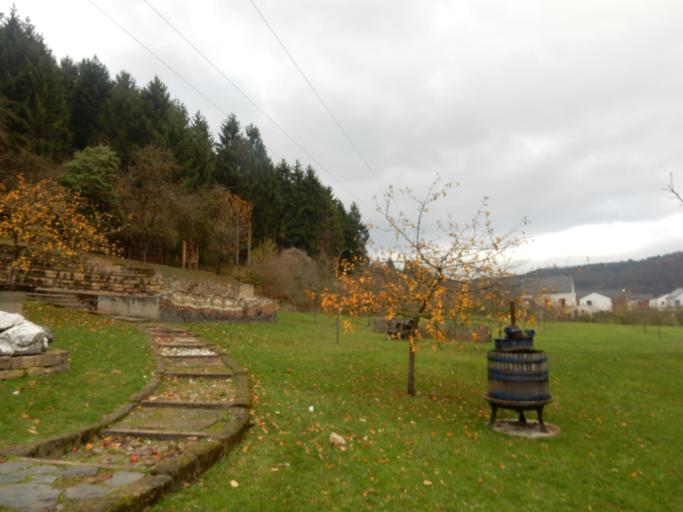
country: LU
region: Grevenmacher
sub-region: Canton d'Echternach
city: Mompach
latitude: 49.7561
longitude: 6.5026
